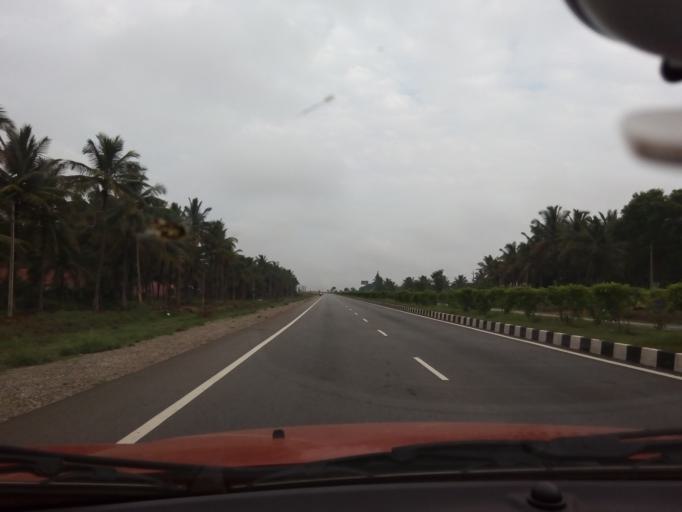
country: IN
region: Karnataka
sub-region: Mandya
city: Belluru
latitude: 12.9582
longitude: 76.6081
